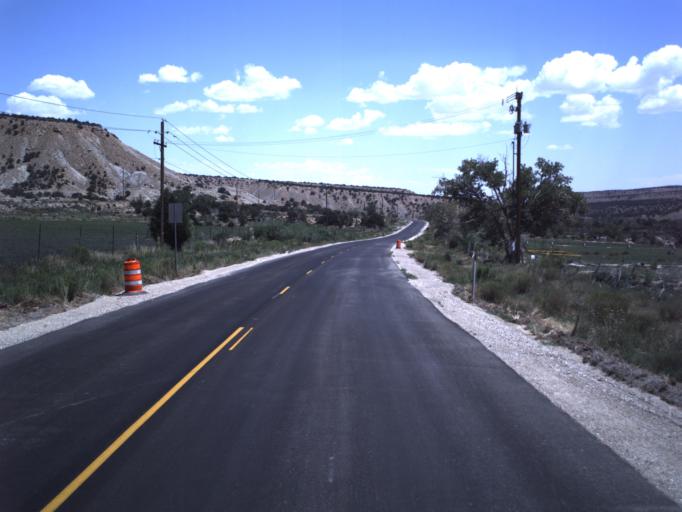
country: US
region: Utah
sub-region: Emery County
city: Orangeville
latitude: 39.2762
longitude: -111.1731
